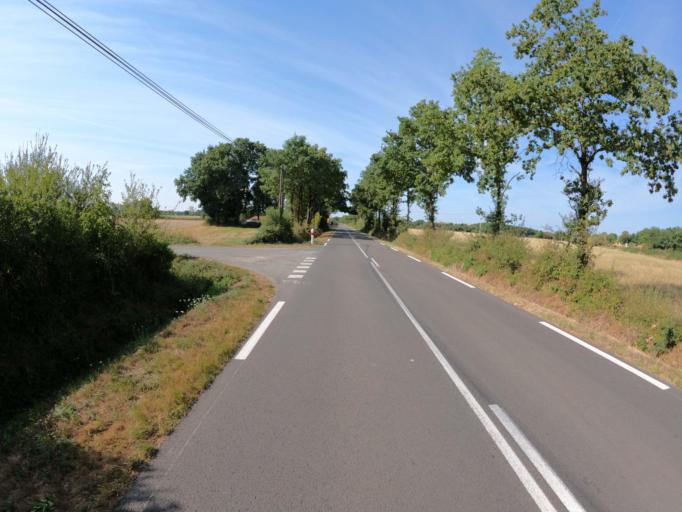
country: FR
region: Pays de la Loire
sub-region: Departement de la Vendee
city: Saint-Christophe-du-Ligneron
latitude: 46.8397
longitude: -1.7502
